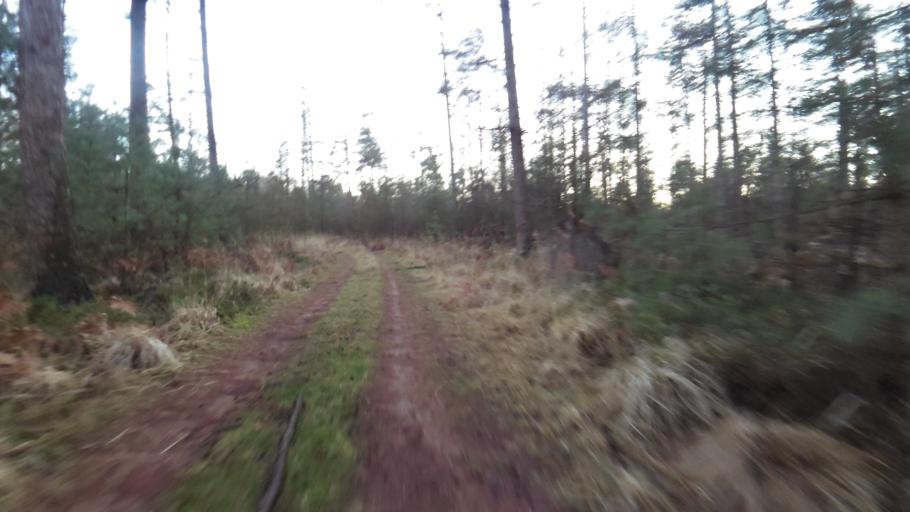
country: NL
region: Gelderland
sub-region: Gemeente Apeldoorn
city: Uddel
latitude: 52.2817
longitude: 5.8540
